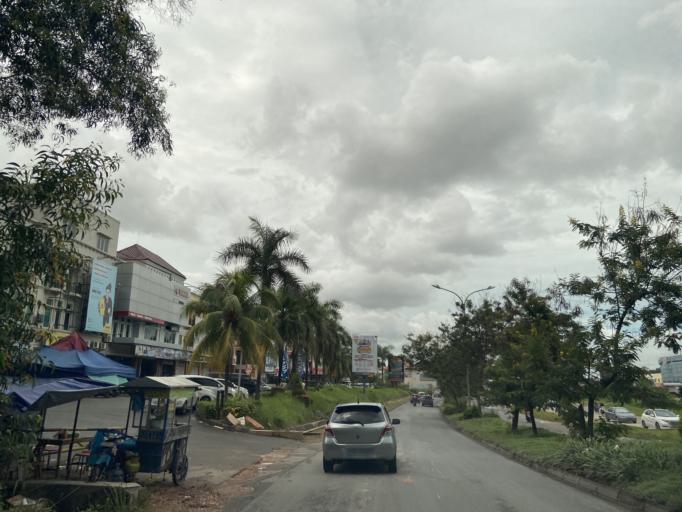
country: SG
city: Singapore
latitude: 1.1386
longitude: 104.0250
